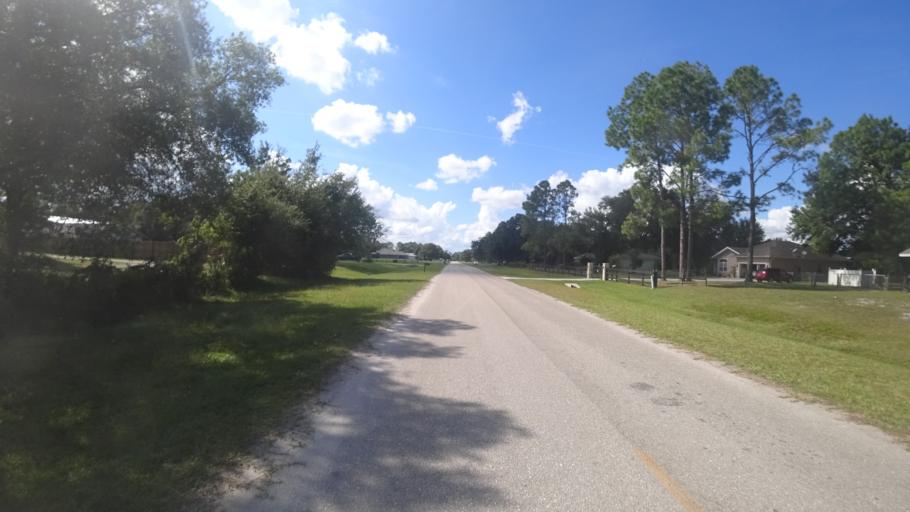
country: US
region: Florida
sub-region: Sarasota County
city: The Meadows
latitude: 27.4683
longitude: -82.3141
